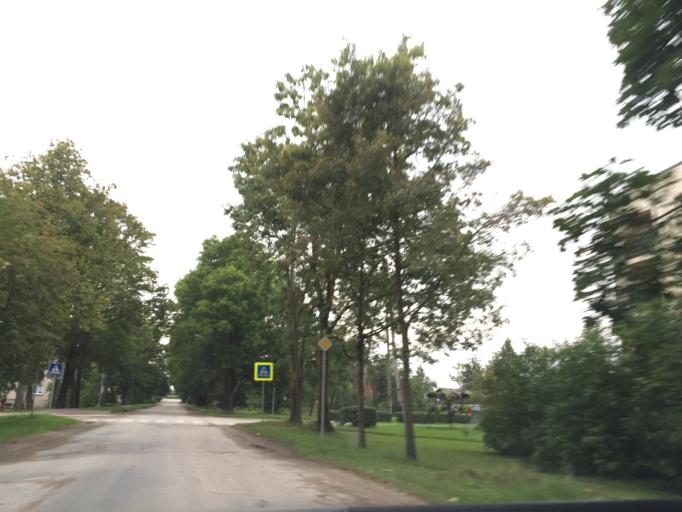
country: LV
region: Varaklani
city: Varaklani
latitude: 56.6091
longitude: 26.7614
